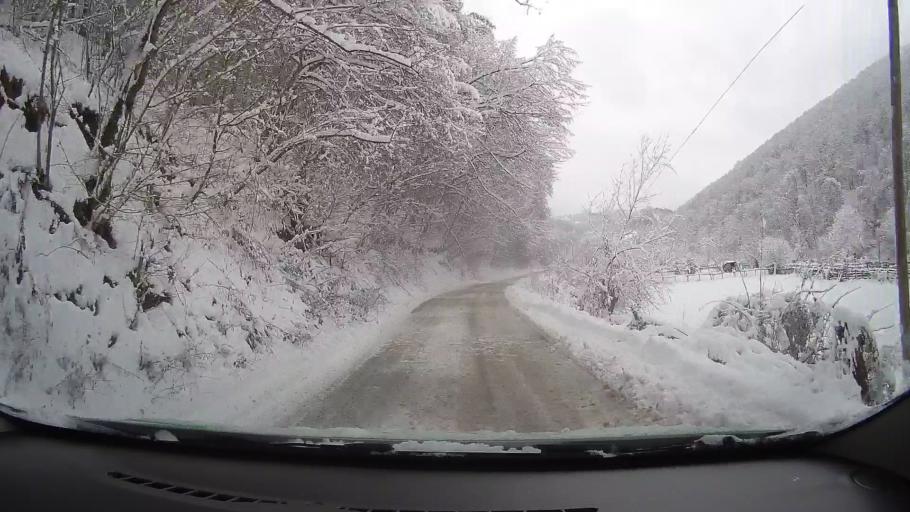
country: RO
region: Alba
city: Pianu de Sus
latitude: 45.8681
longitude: 23.4962
